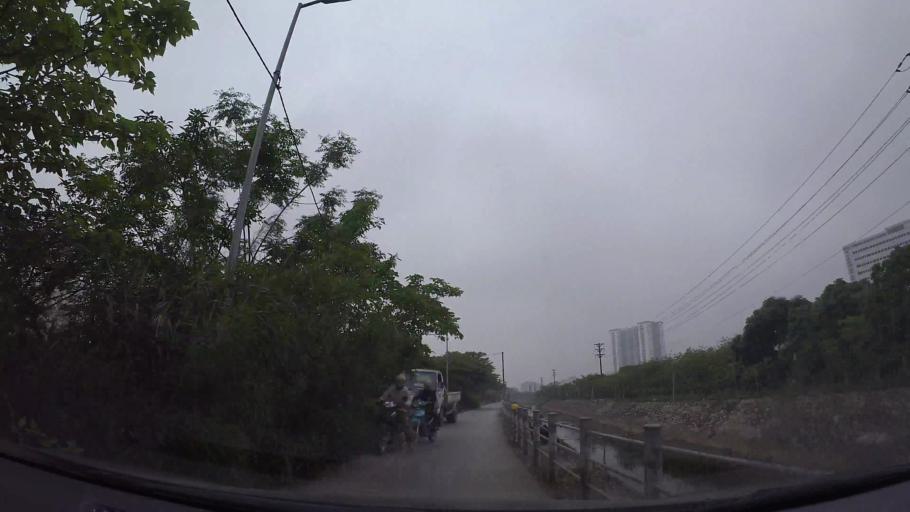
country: VN
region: Ha Noi
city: Van Dien
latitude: 20.9774
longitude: 105.8756
